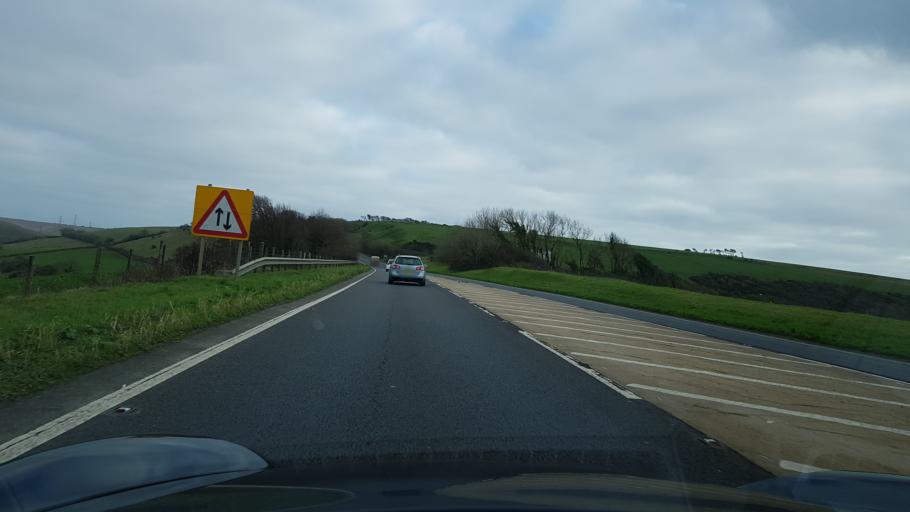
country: GB
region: England
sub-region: Dorset
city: Bridport
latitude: 50.7285
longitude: -2.6744
